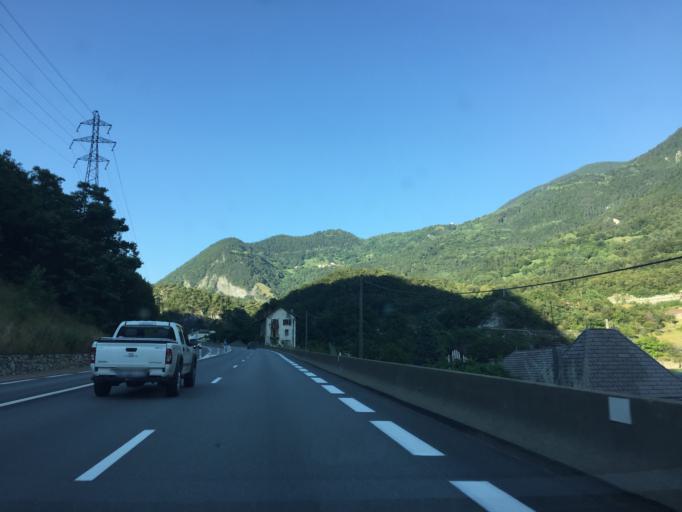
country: FR
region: Rhone-Alpes
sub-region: Departement de la Savoie
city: Moutiers
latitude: 45.4986
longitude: 6.5584
